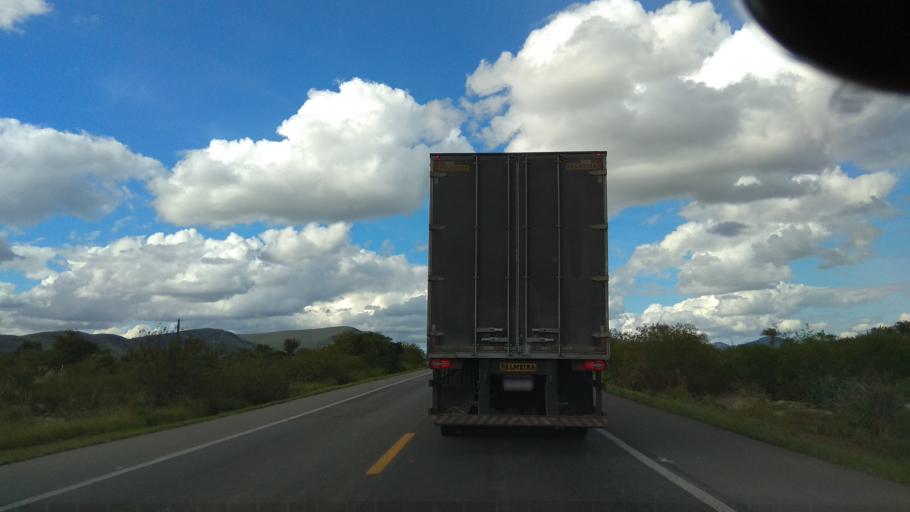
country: BR
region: Bahia
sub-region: Castro Alves
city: Castro Alves
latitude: -12.6754
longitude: -39.6601
